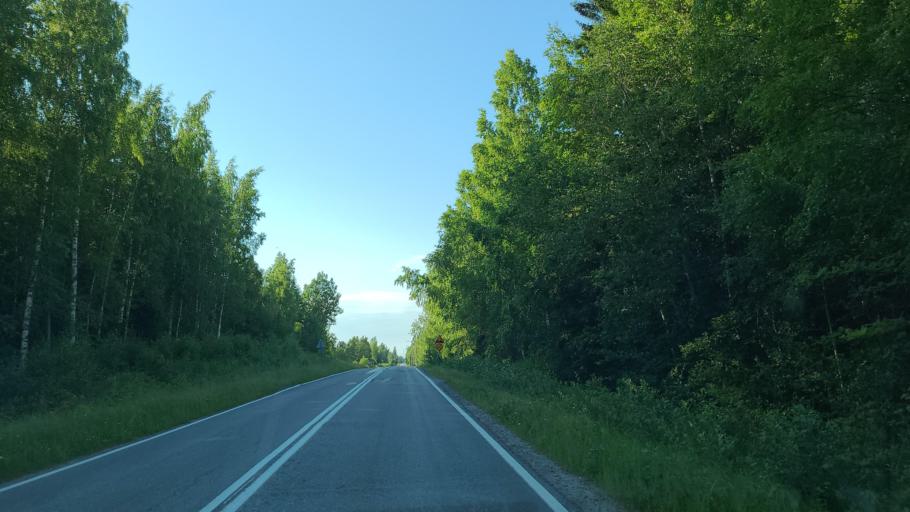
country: FI
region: Ostrobothnia
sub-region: Vaasa
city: Replot
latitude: 63.3231
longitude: 21.3450
